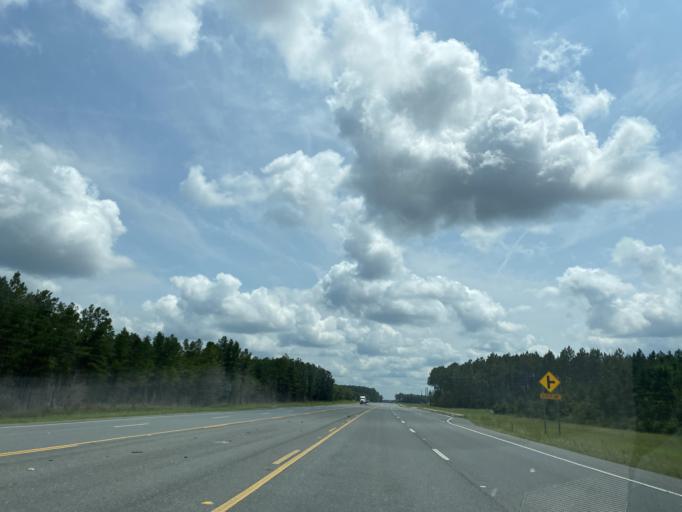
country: US
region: Georgia
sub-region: Ware County
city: Deenwood
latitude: 31.3564
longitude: -82.4637
